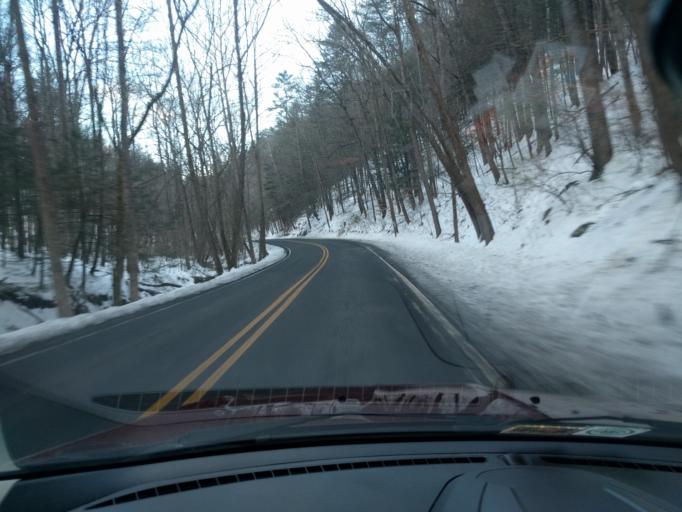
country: US
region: Virginia
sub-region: Bath County
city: Warm Springs
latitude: 38.0750
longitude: -79.8734
